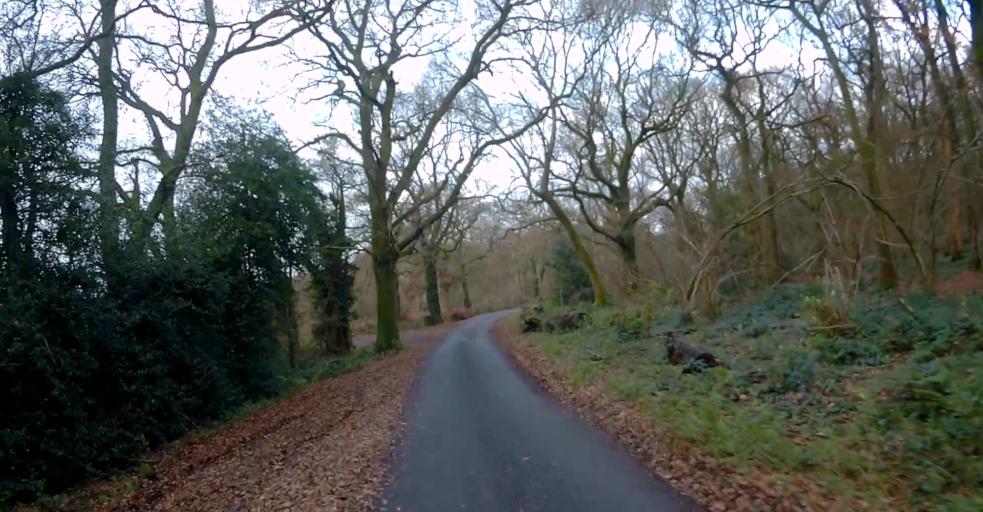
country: GB
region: England
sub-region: Hampshire
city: Basingstoke
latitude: 51.1866
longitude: -1.0970
